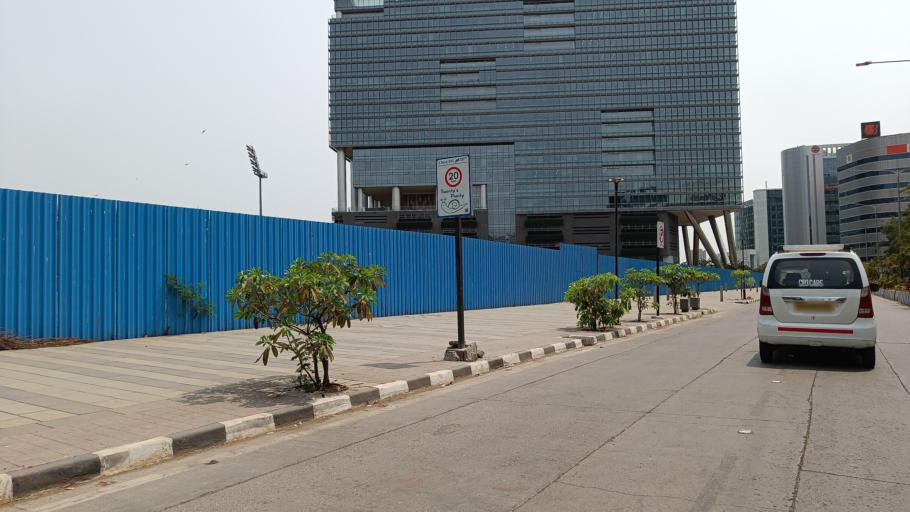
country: IN
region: Maharashtra
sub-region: Mumbai Suburban
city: Mumbai
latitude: 19.0625
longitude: 72.8650
